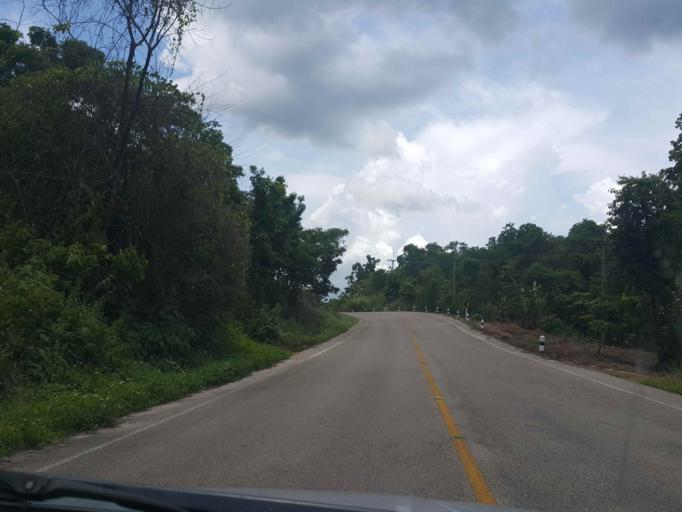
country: TH
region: Phayao
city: Chiang Muan
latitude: 18.9180
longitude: 100.1110
